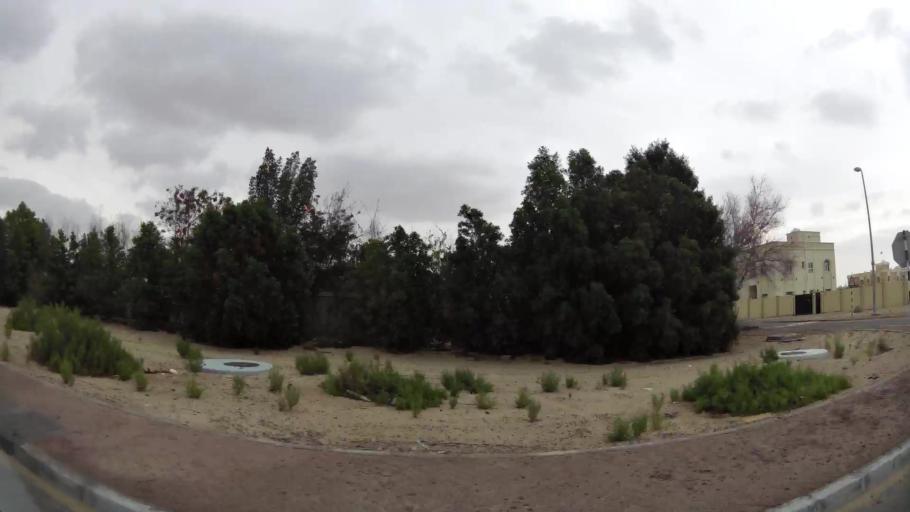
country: AE
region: Abu Dhabi
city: Abu Dhabi
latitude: 24.3742
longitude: 54.6429
